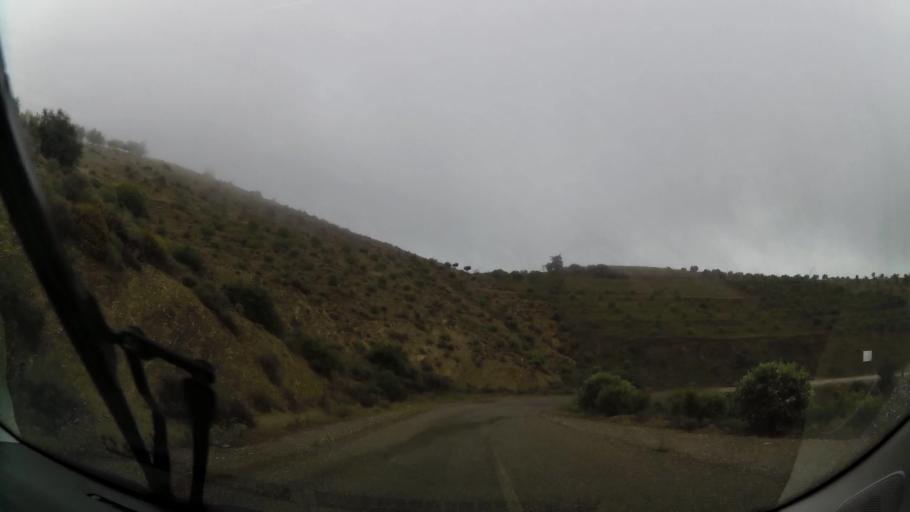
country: MA
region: Taza-Al Hoceima-Taounate
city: Imzourene
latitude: 35.1188
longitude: -3.7772
